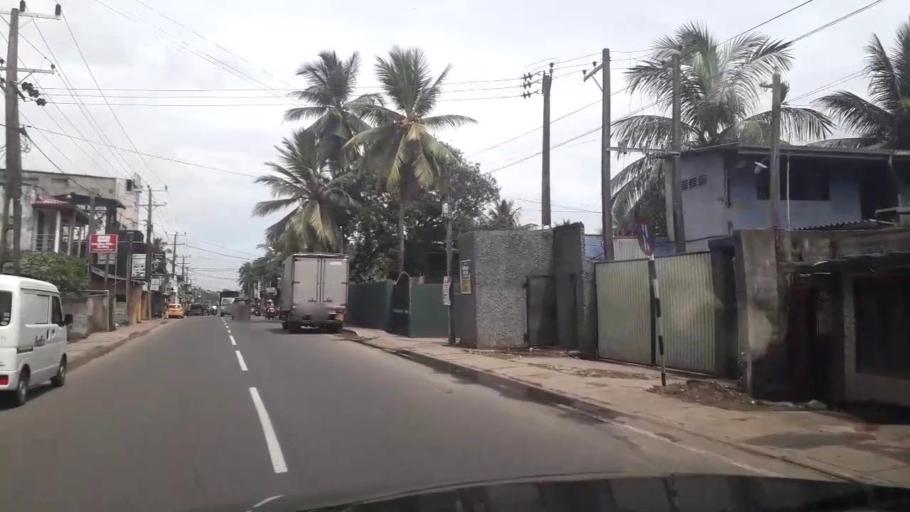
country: LK
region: Western
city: Moratuwa
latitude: 6.7482
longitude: 79.9009
